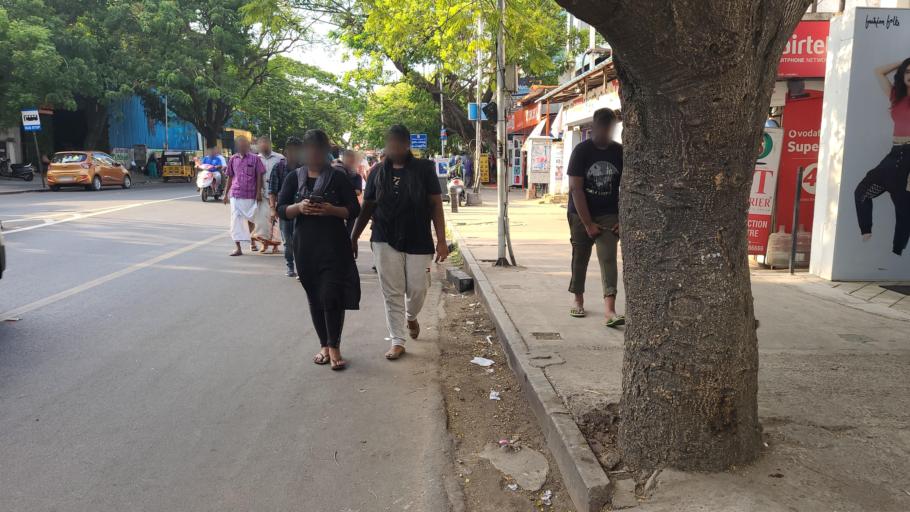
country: IN
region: Tamil Nadu
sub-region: Chennai
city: Gandhi Nagar
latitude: 12.9959
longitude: 80.2677
